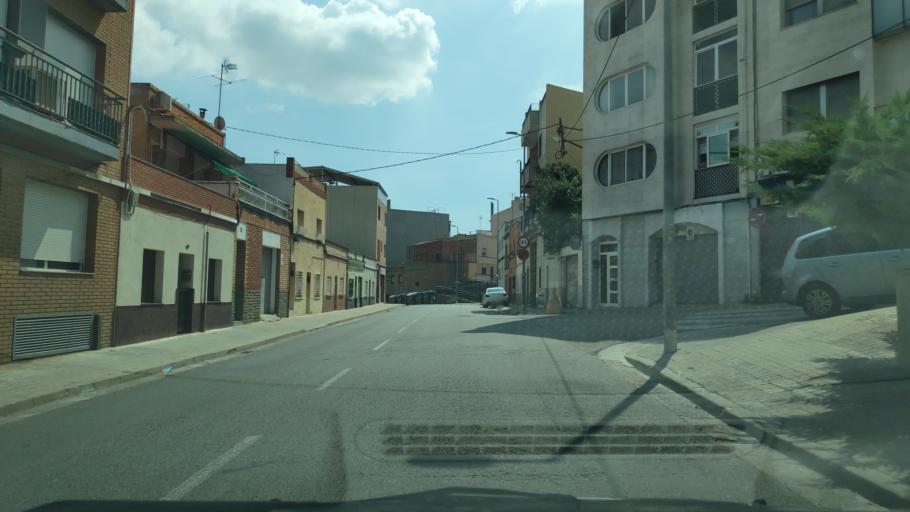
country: ES
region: Catalonia
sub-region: Provincia de Barcelona
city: Sant Quirze del Valles
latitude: 41.5516
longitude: 2.0827
